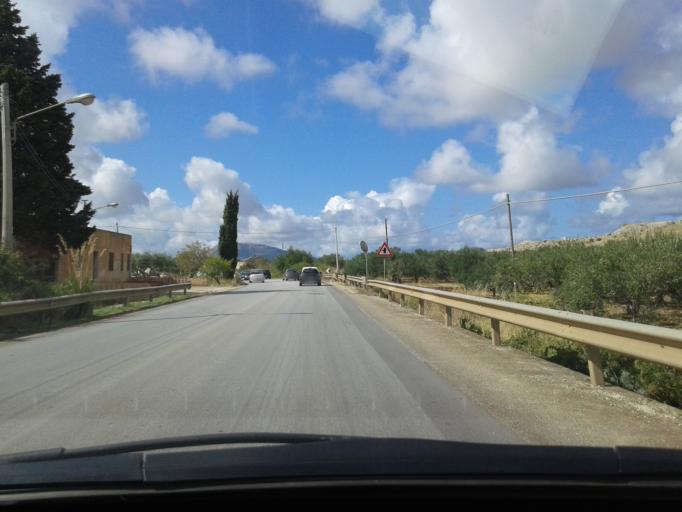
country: IT
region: Sicily
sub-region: Trapani
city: Custonaci
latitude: 38.0789
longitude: 12.7007
